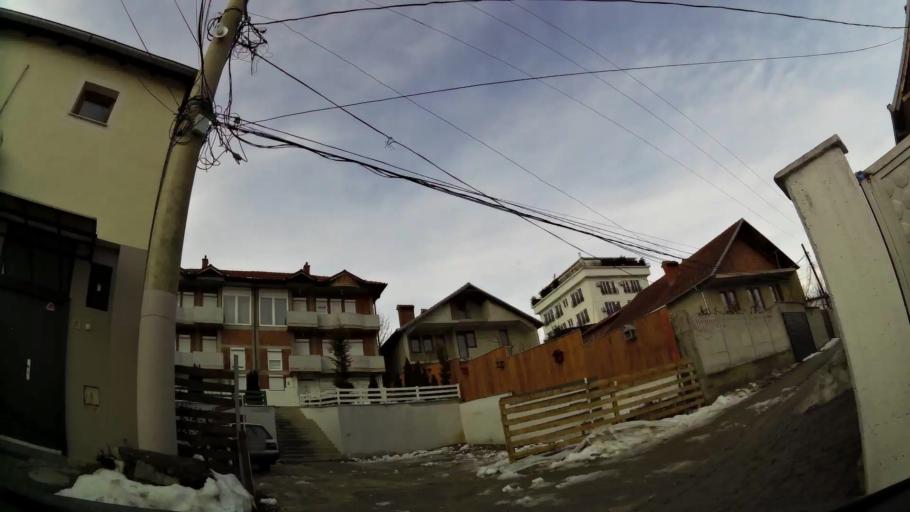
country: XK
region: Pristina
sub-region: Komuna e Prishtines
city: Pristina
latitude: 42.6712
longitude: 21.1846
